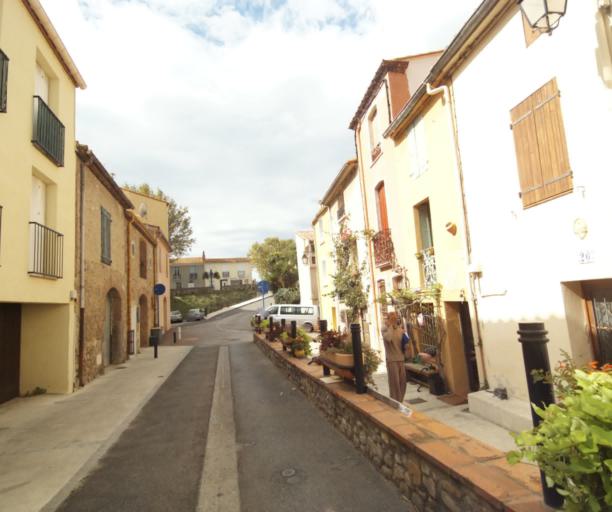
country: FR
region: Languedoc-Roussillon
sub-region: Departement des Pyrenees-Orientales
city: Argelers
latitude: 42.5476
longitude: 3.0214
